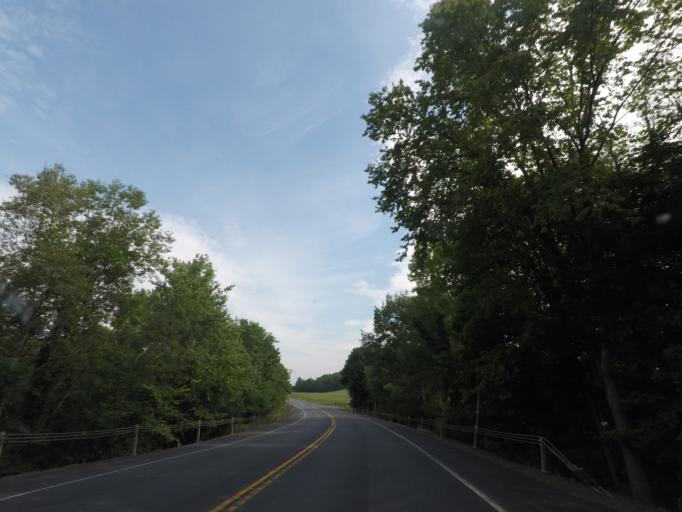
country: US
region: New York
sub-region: Rensselaer County
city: Poestenkill
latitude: 42.6800
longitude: -73.5684
